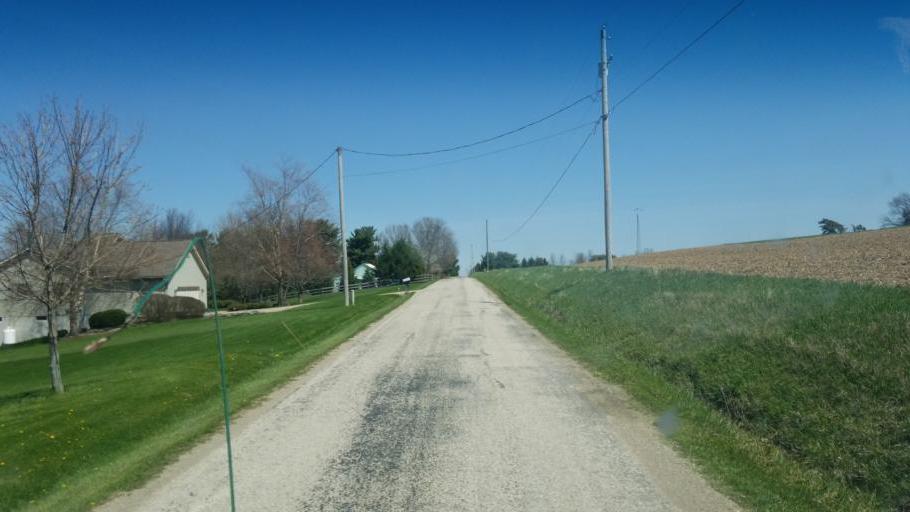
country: US
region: Ohio
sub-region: Ashland County
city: Ashland
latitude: 40.8683
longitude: -82.4161
